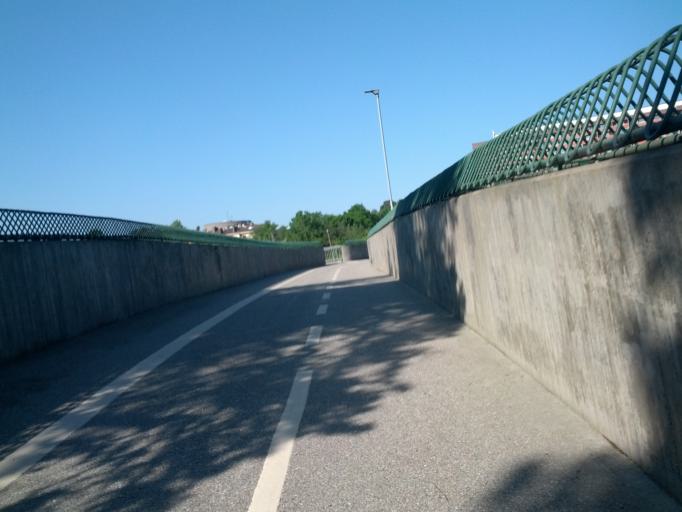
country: SE
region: Stockholm
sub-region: Norrtalje Kommun
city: Bergshamra
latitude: 59.3875
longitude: 18.0446
